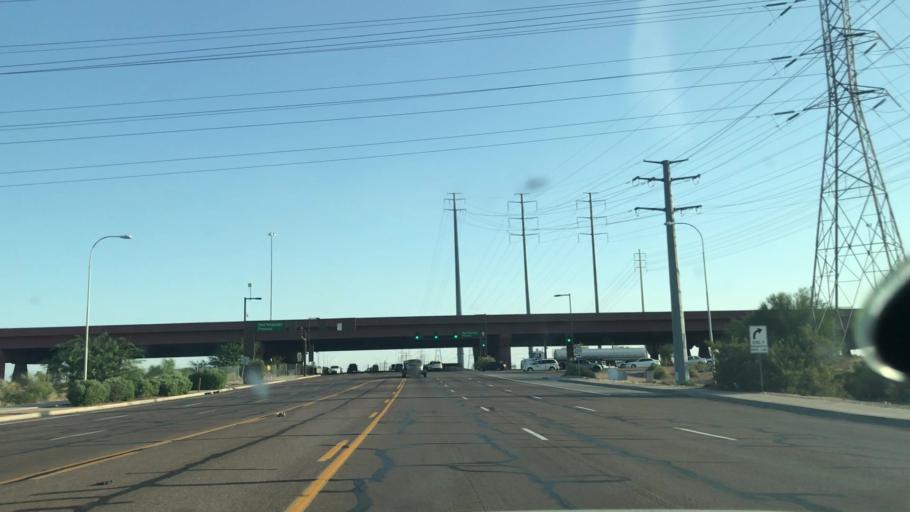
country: US
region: Arizona
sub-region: Maricopa County
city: Tempe
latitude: 33.4376
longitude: -111.9097
